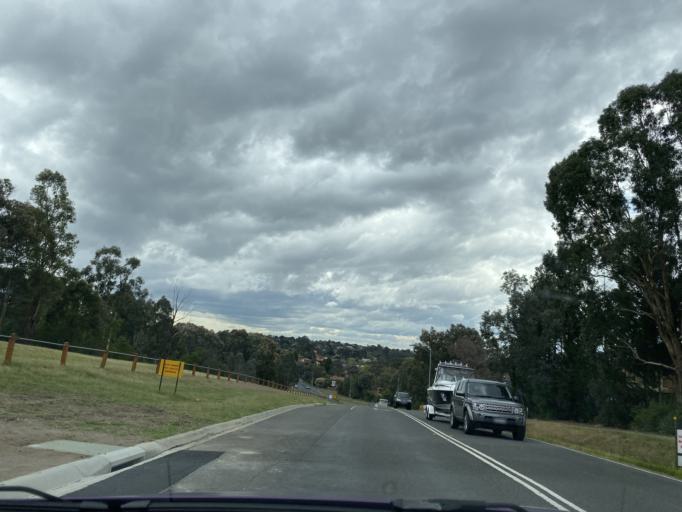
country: AU
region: Victoria
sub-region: Manningham
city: Doncaster East
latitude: -37.7723
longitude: 145.1395
